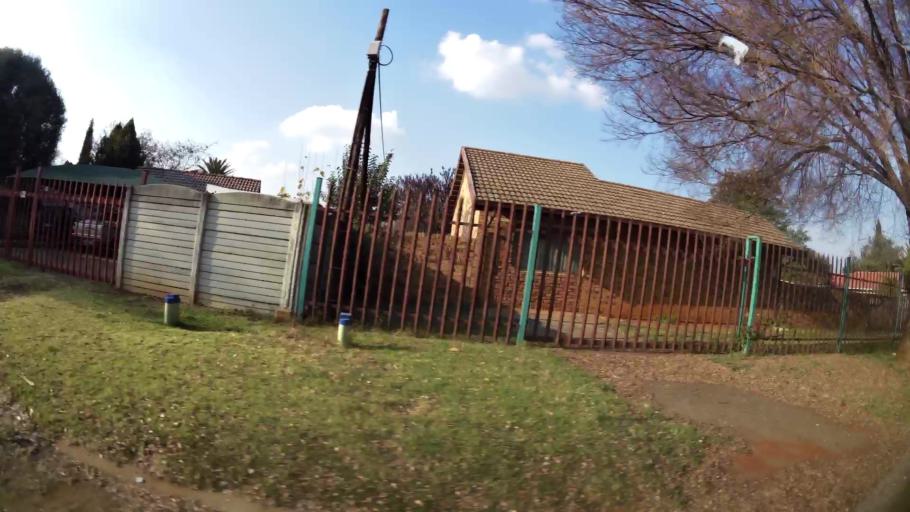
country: ZA
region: Gauteng
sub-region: Ekurhuleni Metropolitan Municipality
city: Benoni
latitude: -26.1286
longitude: 28.3752
